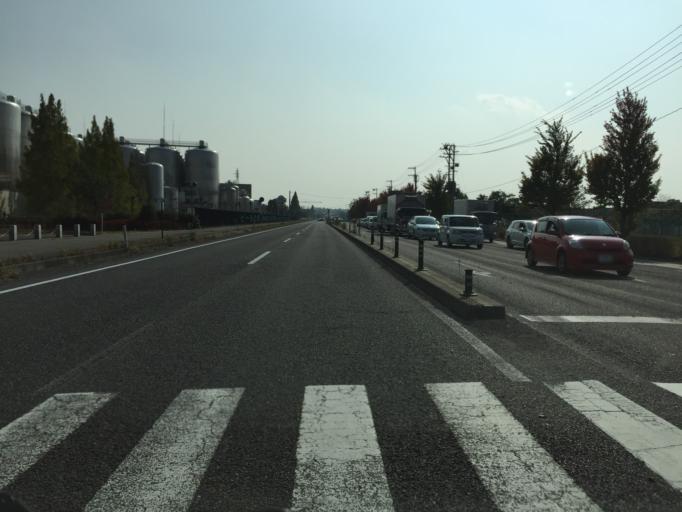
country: JP
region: Fukushima
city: Motomiya
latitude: 37.4821
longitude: 140.3796
